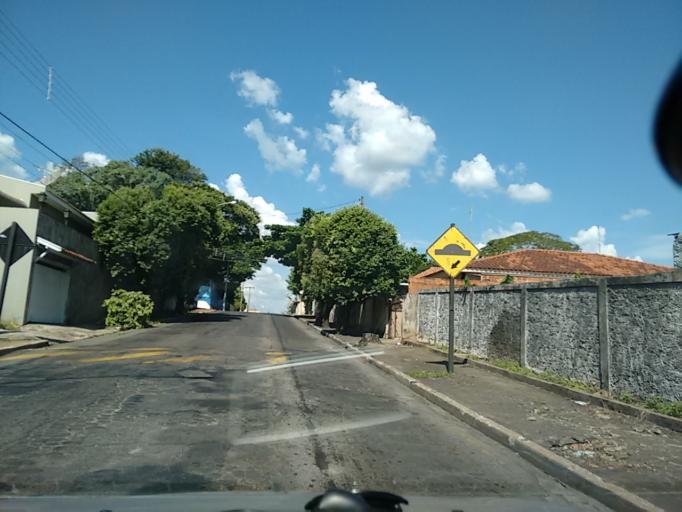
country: BR
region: Sao Paulo
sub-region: Pompeia
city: Pompeia
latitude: -22.1095
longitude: -50.1784
